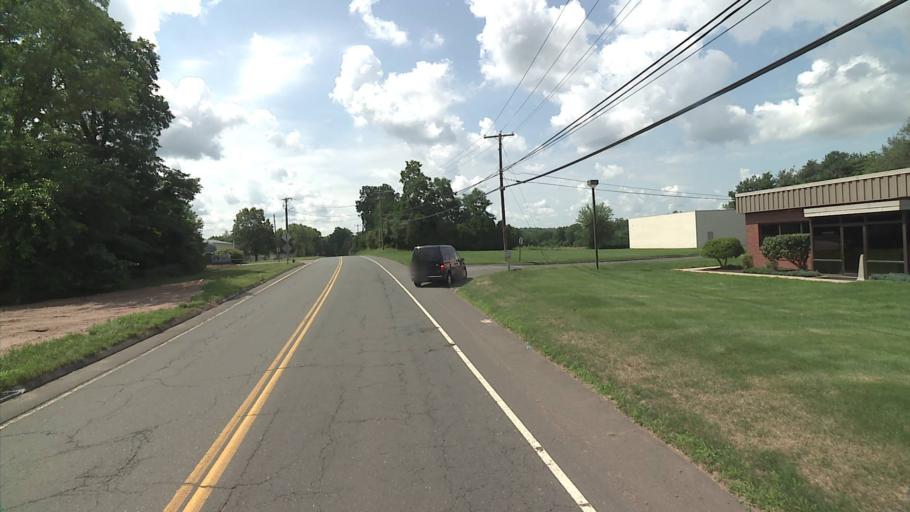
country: US
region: Connecticut
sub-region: Middlesex County
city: Cromwell
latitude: 41.6075
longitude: -72.6028
